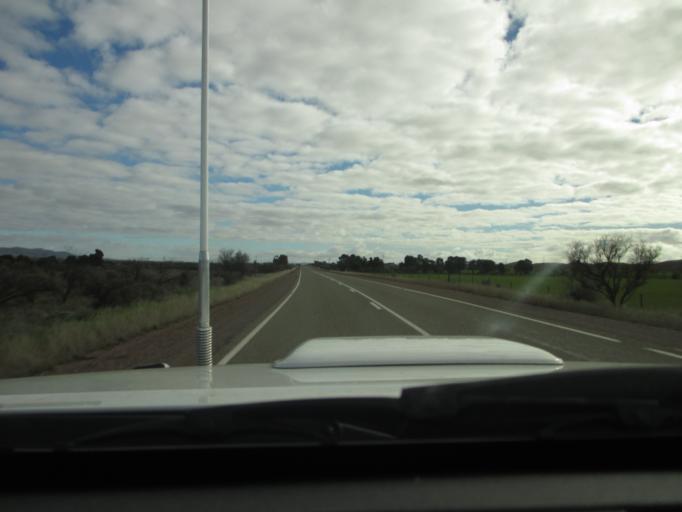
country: AU
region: South Australia
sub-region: Flinders Ranges
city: Quorn
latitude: -32.4367
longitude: 138.5347
